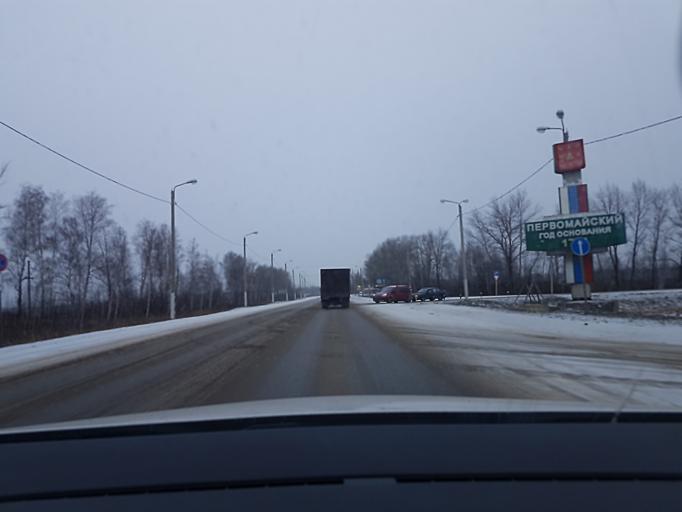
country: RU
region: Tambov
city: Pervomayskiy
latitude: 53.2453
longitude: 40.2542
